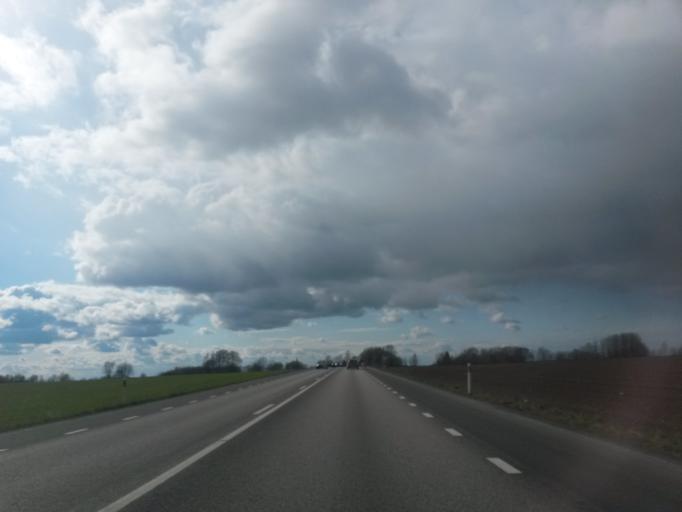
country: SE
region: Vaestra Goetaland
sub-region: Skara Kommun
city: Axvall
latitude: 58.3831
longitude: 13.6721
